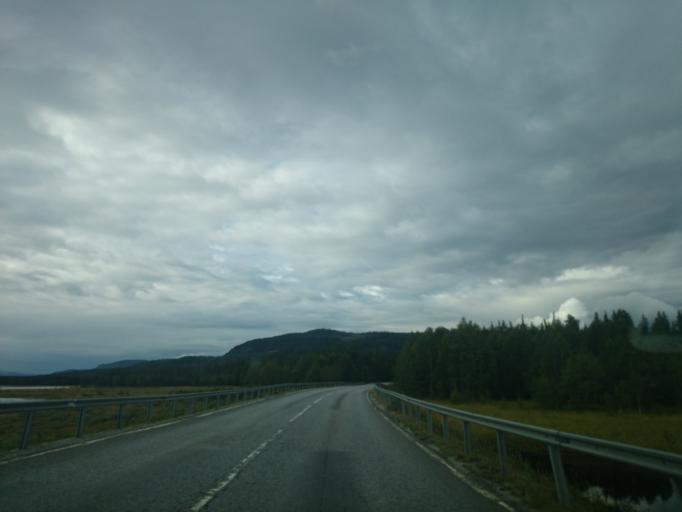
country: NO
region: Hedmark
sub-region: Engerdal
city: Engerdal
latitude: 62.4279
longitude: 12.7194
